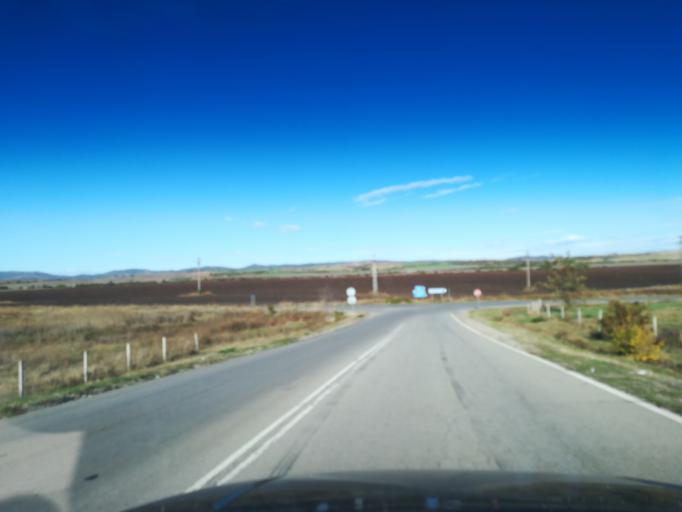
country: BG
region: Stara Zagora
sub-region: Obshtina Chirpan
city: Chirpan
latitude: 42.2080
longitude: 25.3006
